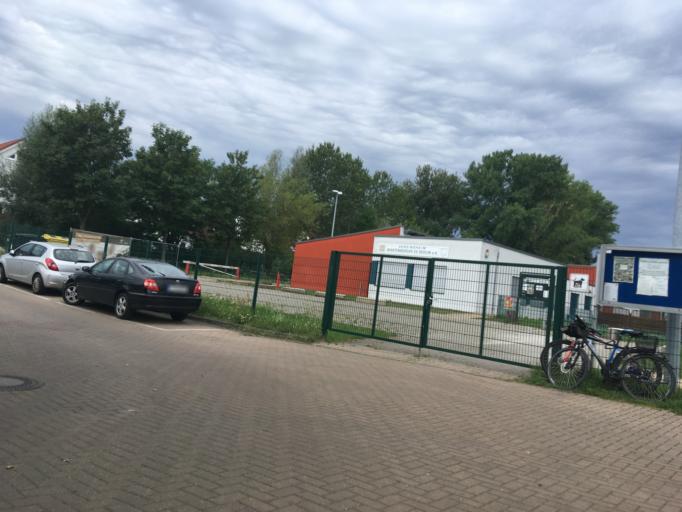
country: DE
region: Berlin
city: Wartenberg
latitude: 52.5774
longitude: 13.5146
